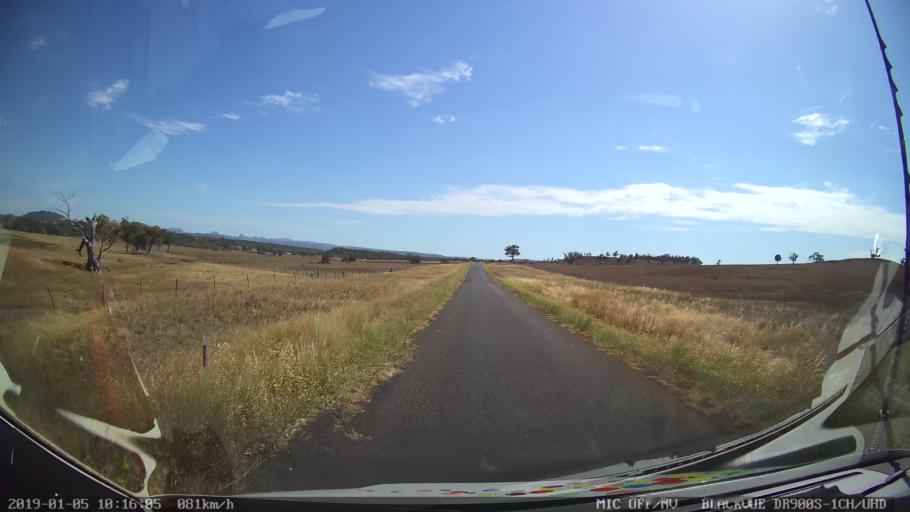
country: AU
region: New South Wales
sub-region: Gilgandra
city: Gilgandra
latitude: -31.5785
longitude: 148.9493
